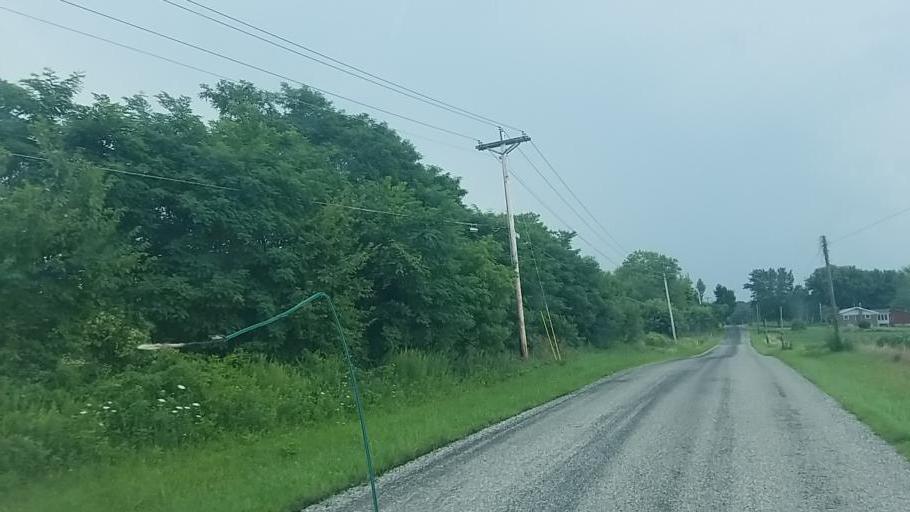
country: US
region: Ohio
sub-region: Medina County
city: Lodi
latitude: 40.9954
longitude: -82.0058
